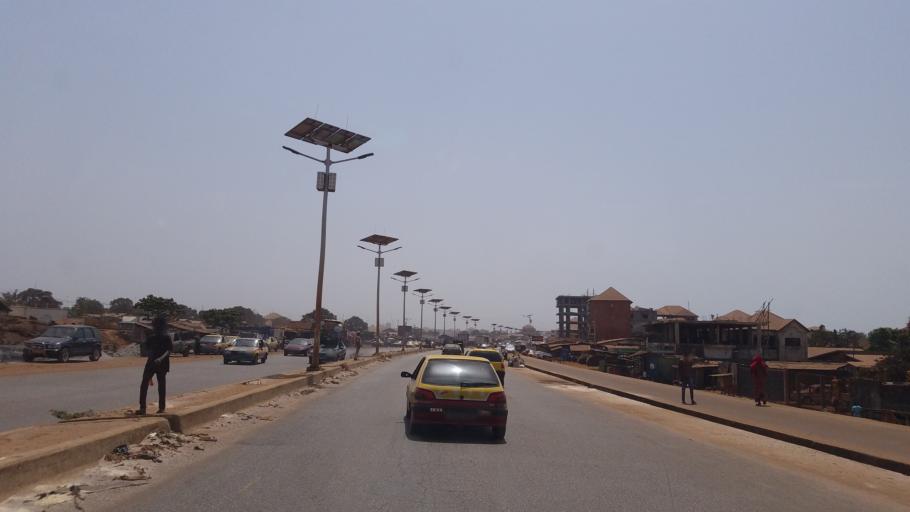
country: GN
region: Kindia
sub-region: Prefecture de Dubreka
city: Dubreka
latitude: 9.6580
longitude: -13.5679
